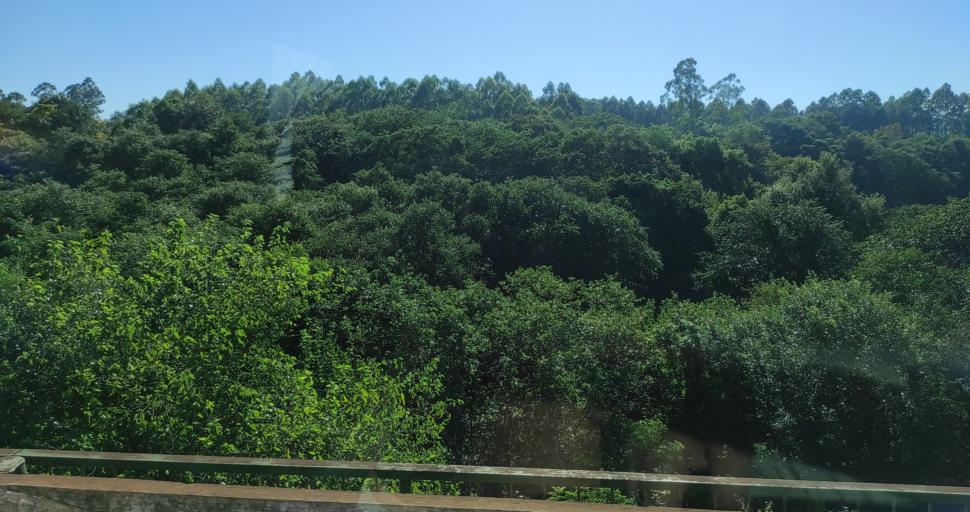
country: AR
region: Misiones
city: El Soberbio
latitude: -27.2796
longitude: -54.1966
